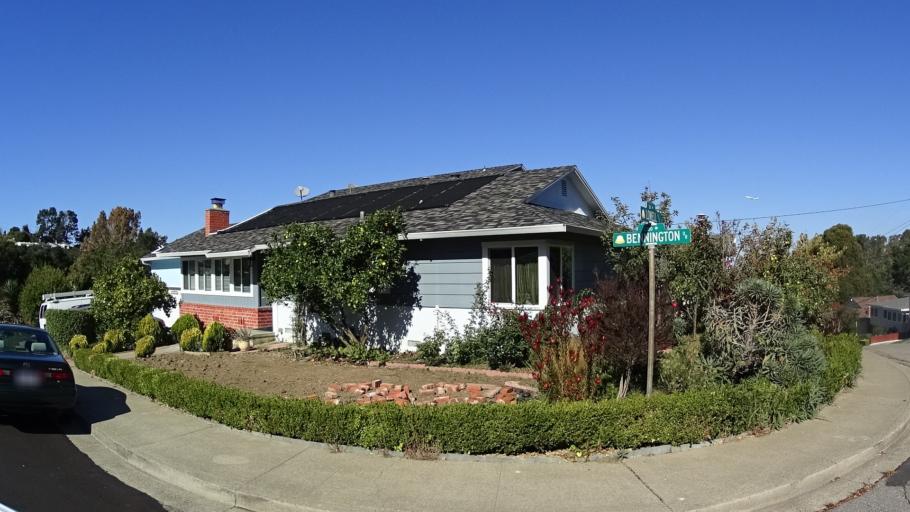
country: US
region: California
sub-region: San Mateo County
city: San Bruno
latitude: 37.6130
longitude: -122.4318
